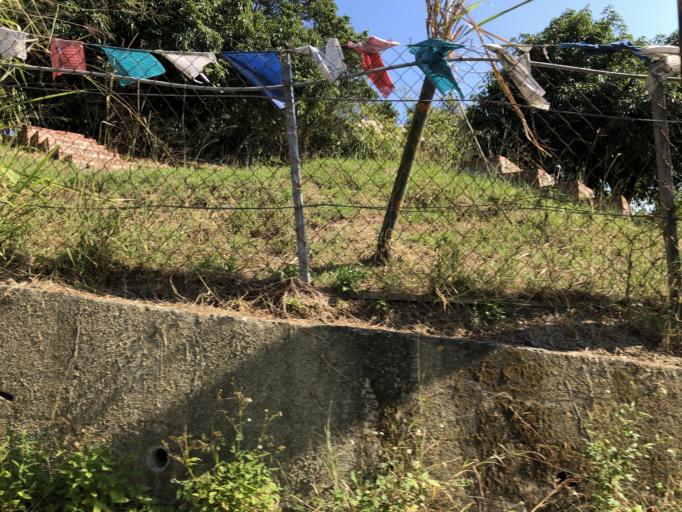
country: TW
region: Taiwan
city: Yujing
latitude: 23.0520
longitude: 120.3808
